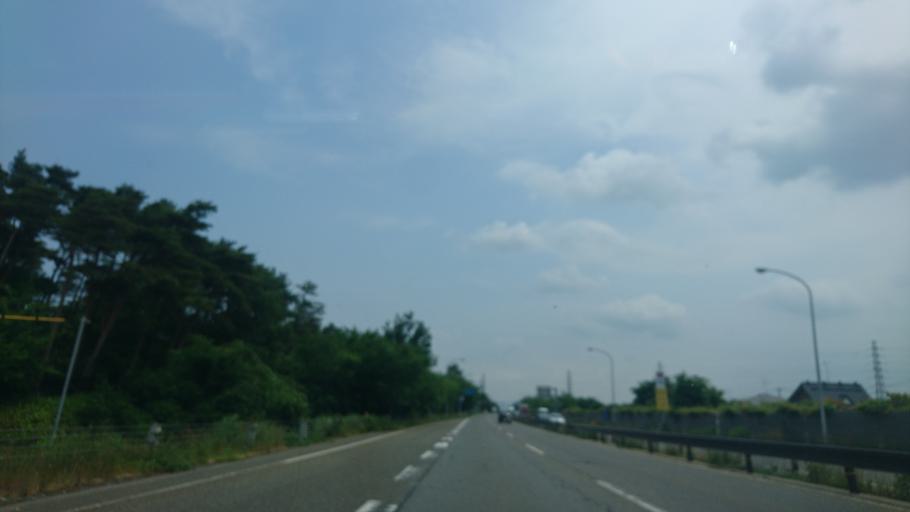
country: JP
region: Niigata
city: Kameda-honcho
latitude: 37.9440
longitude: 139.1873
